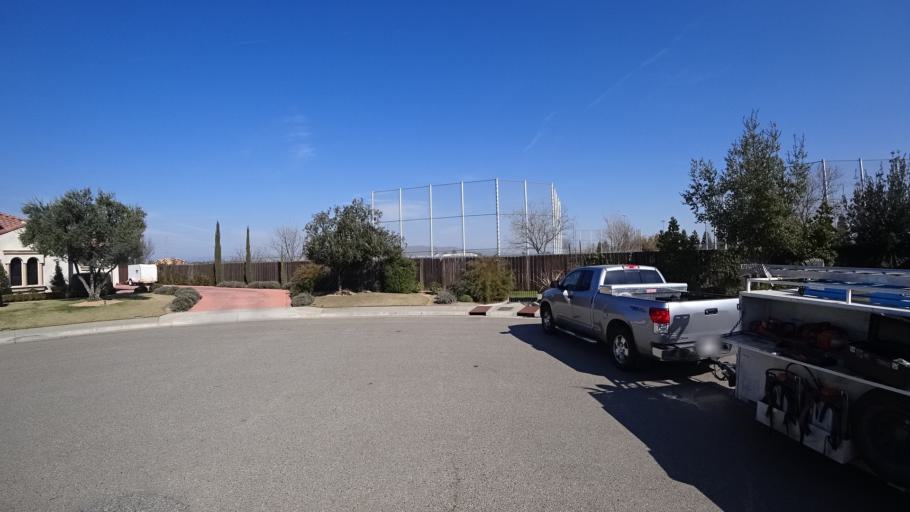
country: US
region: California
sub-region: Fresno County
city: Clovis
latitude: 36.8931
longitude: -119.7370
